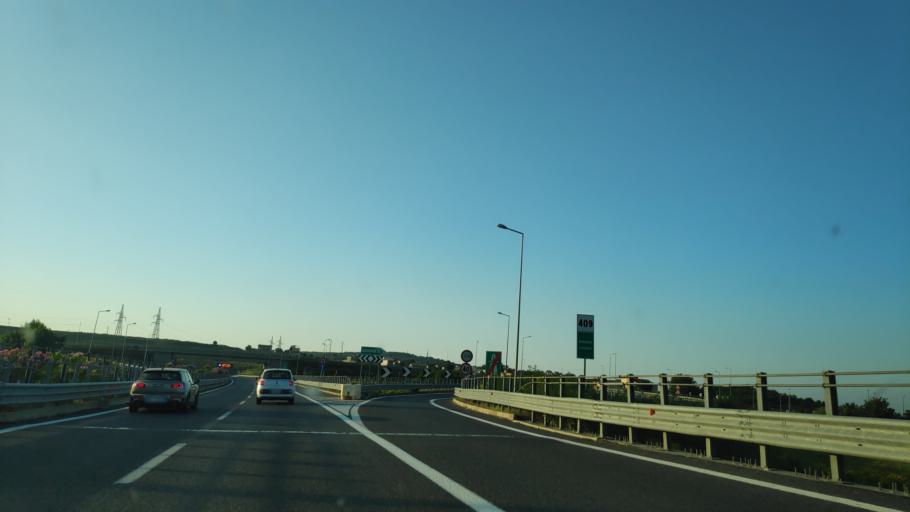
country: IT
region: Calabria
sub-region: Provincia di Reggio Calabria
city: Ceramida-Pellegrina
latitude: 38.3090
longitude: 15.8444
